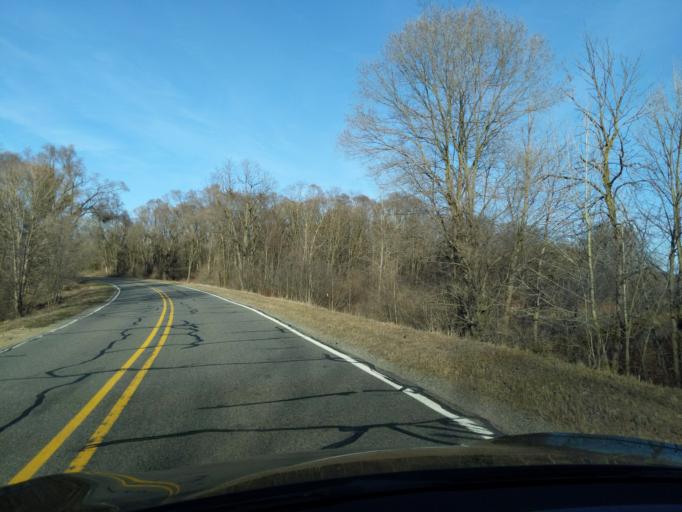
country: US
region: Michigan
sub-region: Ionia County
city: Saranac
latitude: 42.9439
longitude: -85.1687
